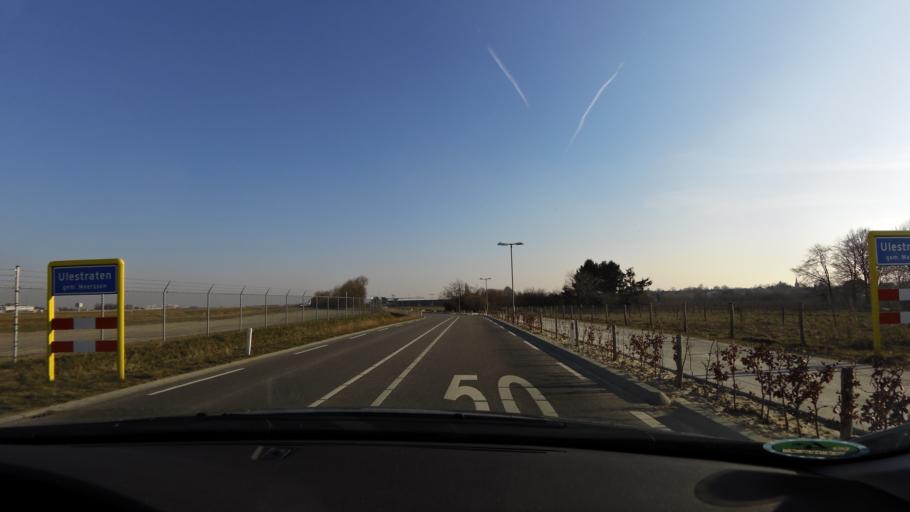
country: NL
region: Limburg
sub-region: Gemeente Meerssen
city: Meerssen
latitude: 50.9059
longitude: 5.7674
